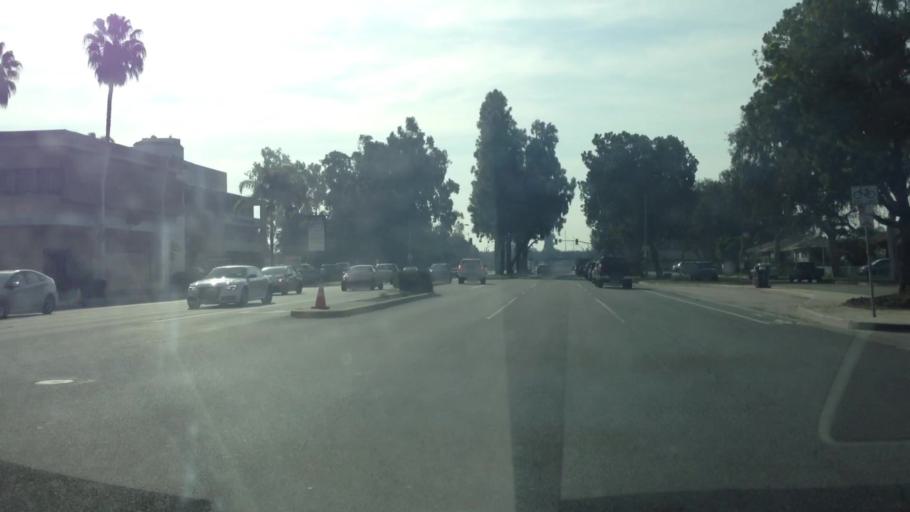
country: US
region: California
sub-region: Los Angeles County
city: Signal Hill
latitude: 33.8068
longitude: -118.1254
